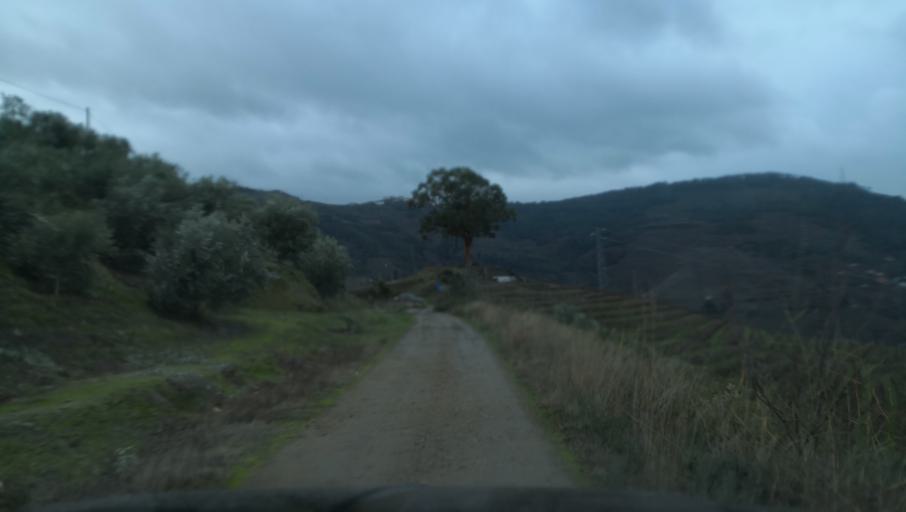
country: PT
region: Vila Real
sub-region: Santa Marta de Penaguiao
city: Santa Marta de Penaguiao
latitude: 41.2376
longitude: -7.7468
